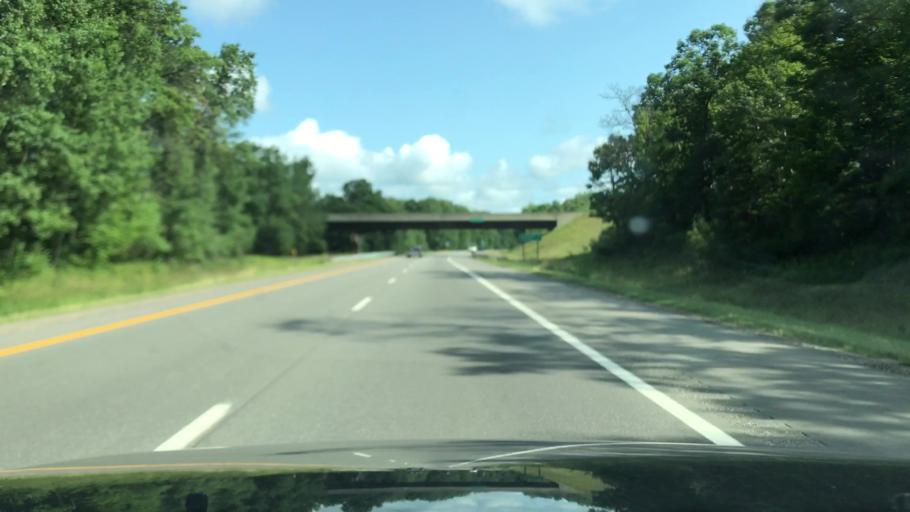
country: US
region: Michigan
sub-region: Montcalm County
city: Howard City
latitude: 43.4378
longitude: -85.4925
